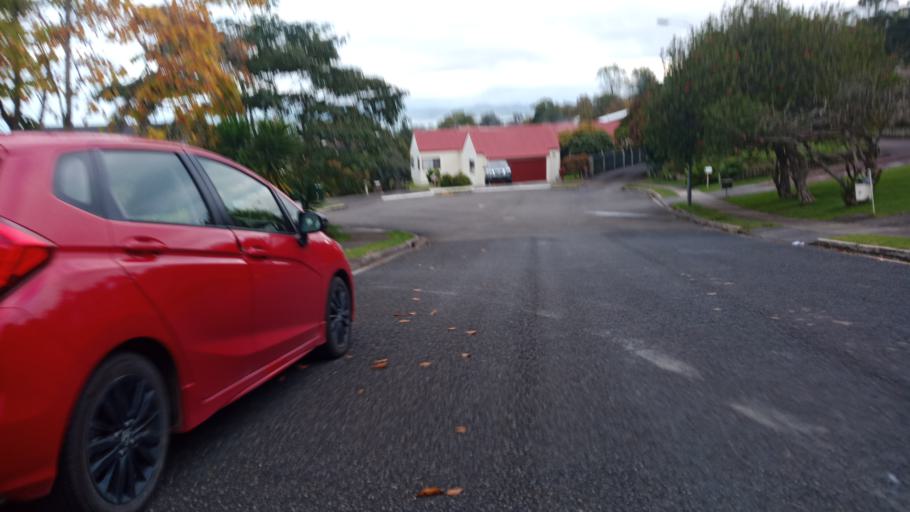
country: NZ
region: Gisborne
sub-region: Gisborne District
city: Gisborne
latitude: -38.6492
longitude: 178.0296
